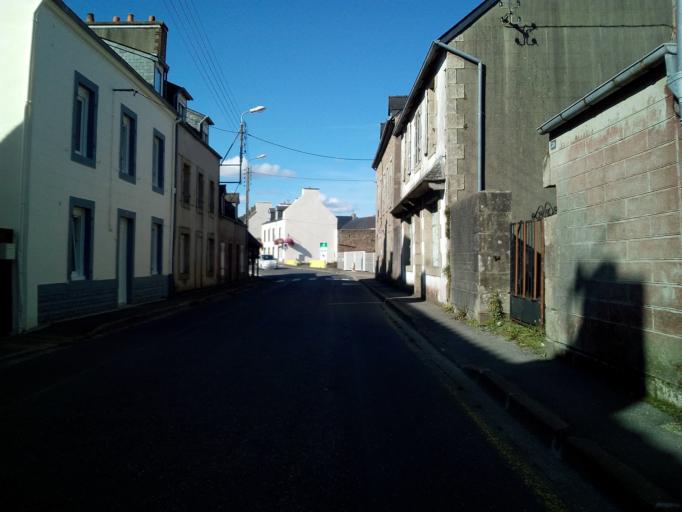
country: FR
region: Brittany
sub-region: Departement du Finistere
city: Landivisiau
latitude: 48.5070
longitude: -4.0729
